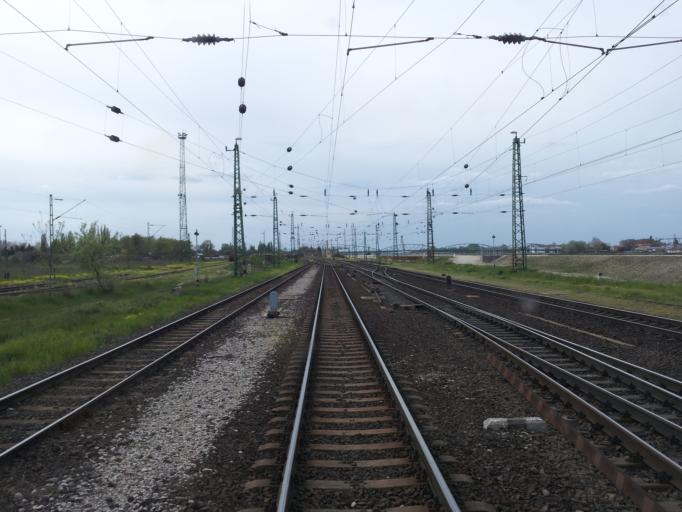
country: HU
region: Komarom-Esztergom
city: Komarom
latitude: 47.7471
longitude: 18.1337
